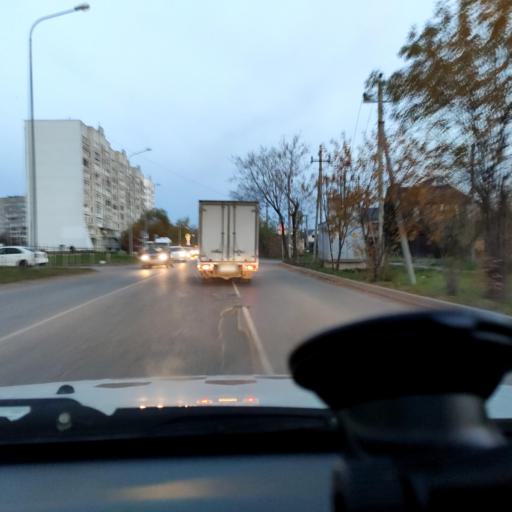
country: RU
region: Perm
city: Perm
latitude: 58.0059
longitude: 56.3267
